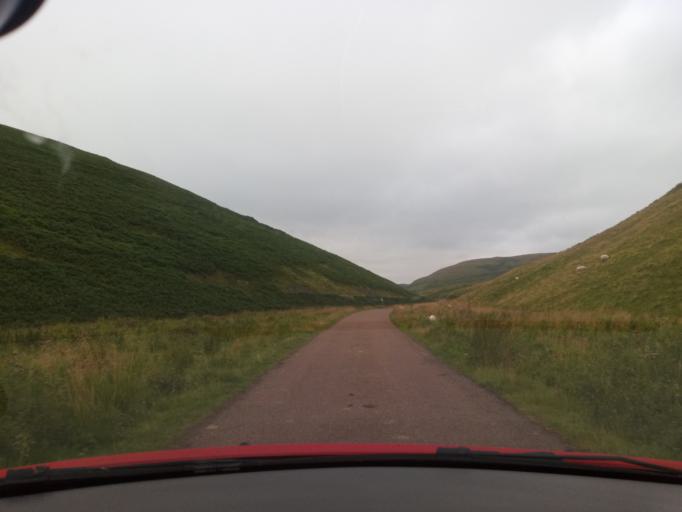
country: GB
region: England
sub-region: Northumberland
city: Rochester
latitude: 55.3692
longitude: -2.2090
